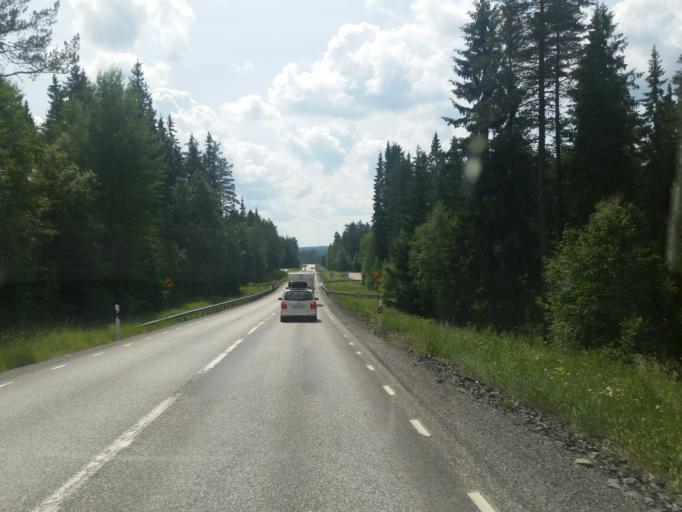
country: SE
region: OErebro
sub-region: Ljusnarsbergs Kommun
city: Kopparberg
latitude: 59.9038
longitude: 15.0205
